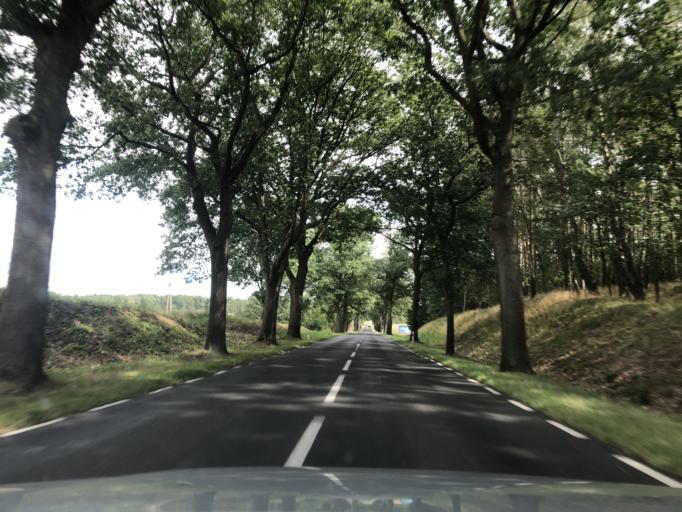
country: PL
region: Greater Poland Voivodeship
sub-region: Powiat czarnkowsko-trzcianecki
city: Trzcianka
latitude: 53.0681
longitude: 16.5487
